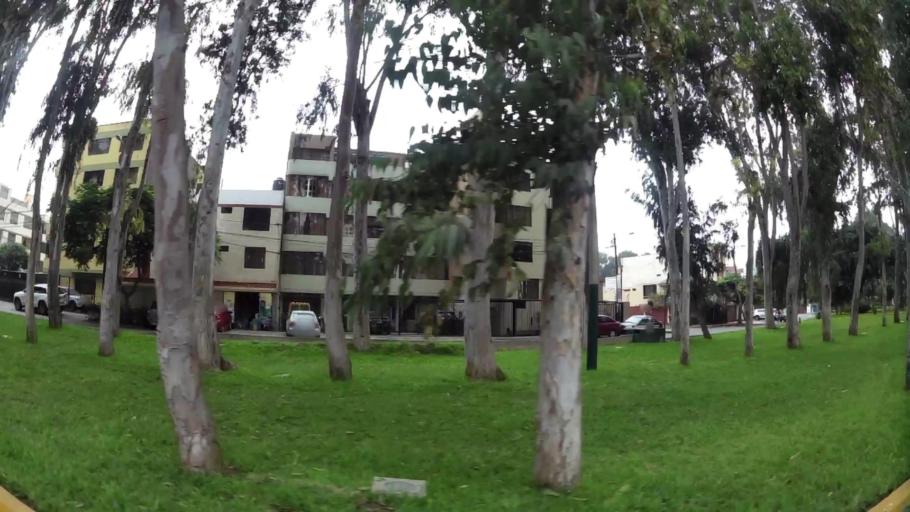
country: PE
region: Lima
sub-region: Lima
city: Surco
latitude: -12.1400
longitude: -76.9918
